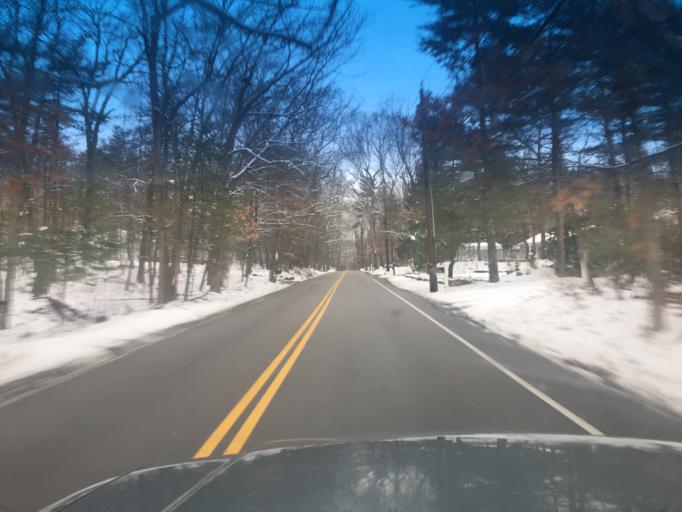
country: US
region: Massachusetts
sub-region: Norfolk County
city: Millis
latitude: 42.1915
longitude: -71.3797
